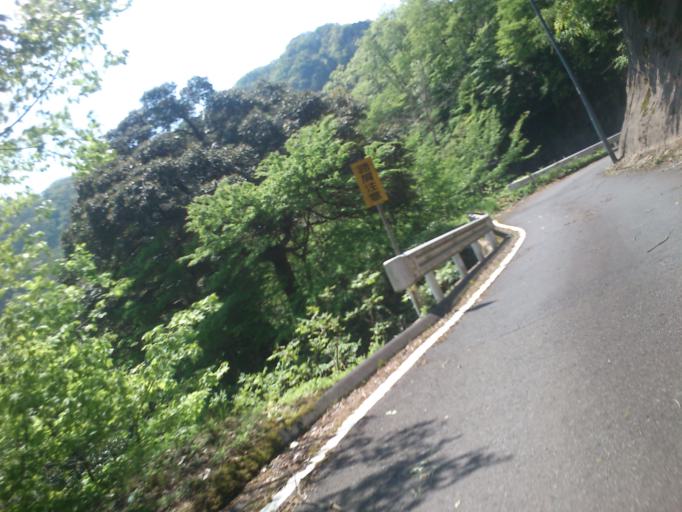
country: JP
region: Kyoto
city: Miyazu
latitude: 35.6991
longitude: 135.1570
